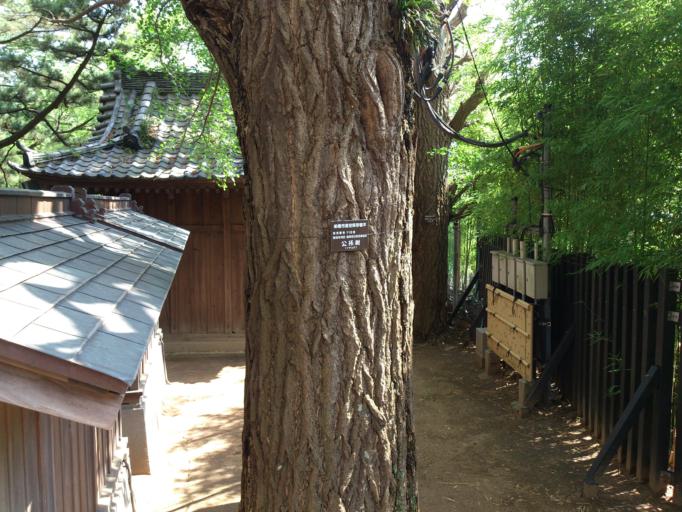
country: JP
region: Chiba
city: Funabashi
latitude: 35.6963
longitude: 139.9927
